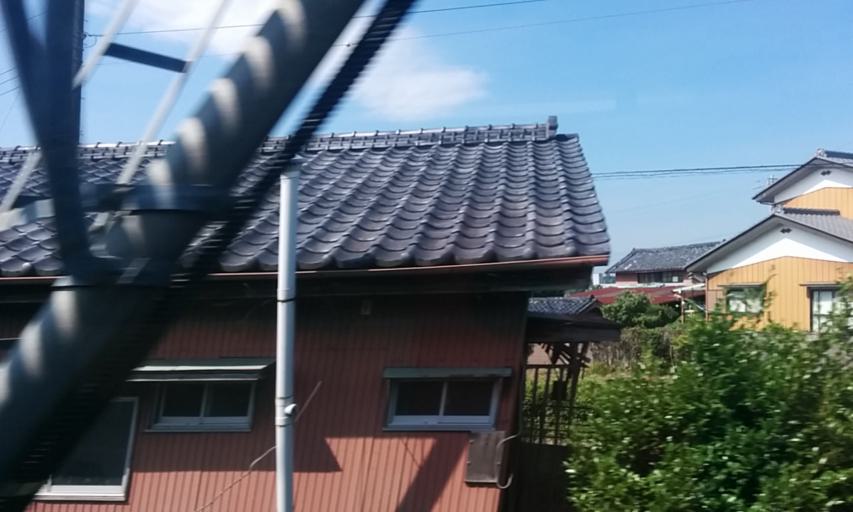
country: JP
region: Saitama
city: Kazo
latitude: 36.1403
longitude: 139.5703
